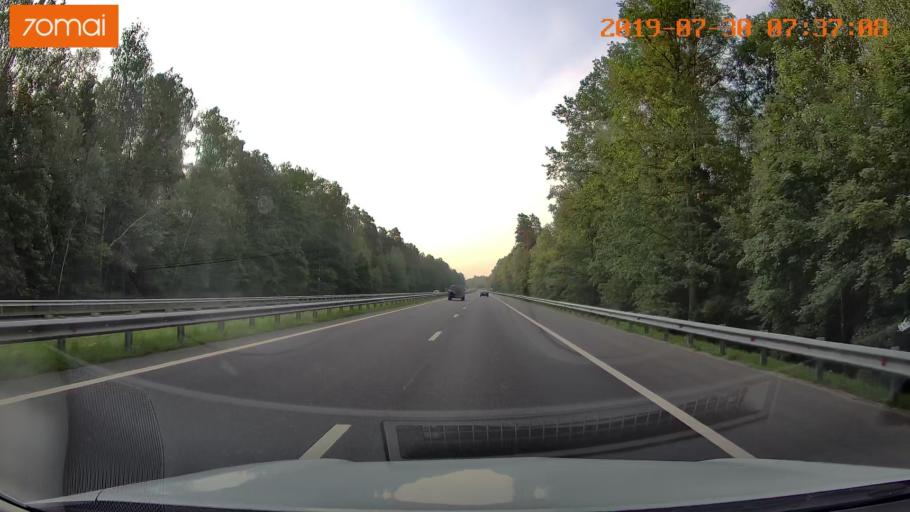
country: RU
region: Kaliningrad
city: Gvardeysk
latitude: 54.6583
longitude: 21.1401
